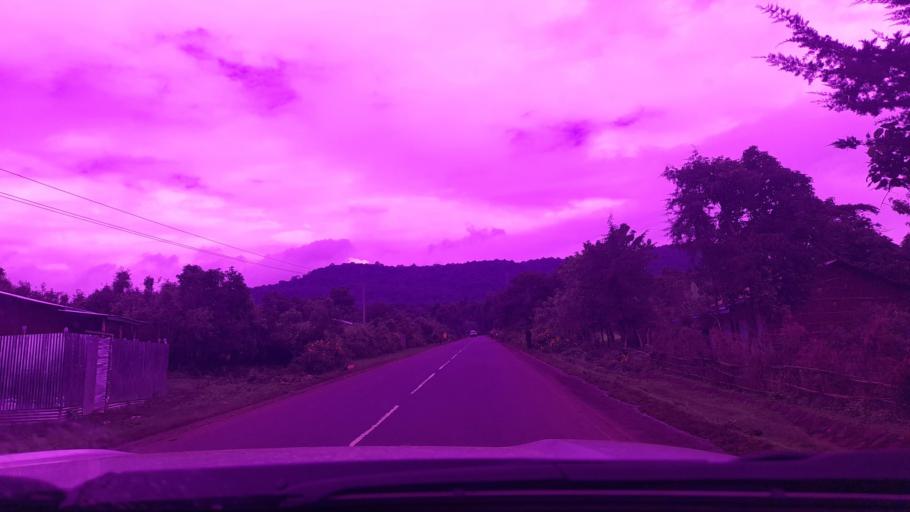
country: ET
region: Oromiya
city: Jima
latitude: 7.5578
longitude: 36.6061
